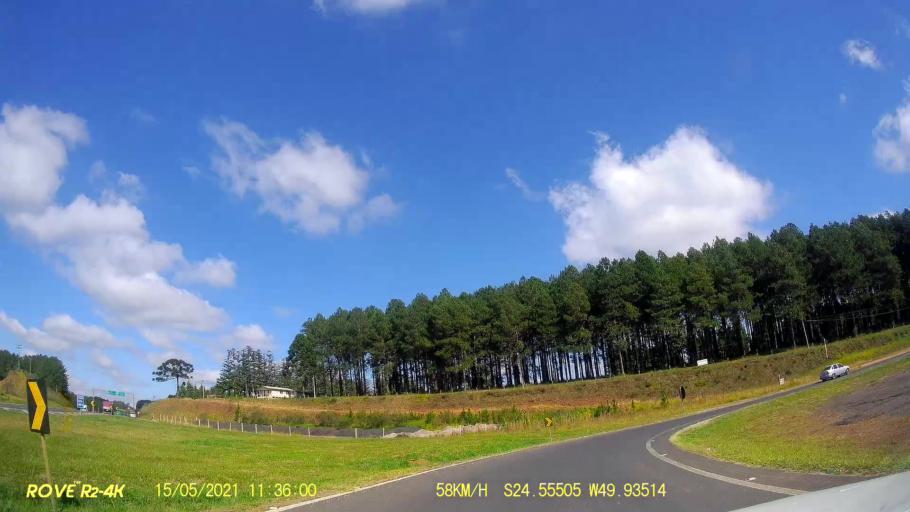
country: BR
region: Parana
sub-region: Pirai Do Sul
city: Pirai do Sul
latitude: -24.5547
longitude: -49.9350
